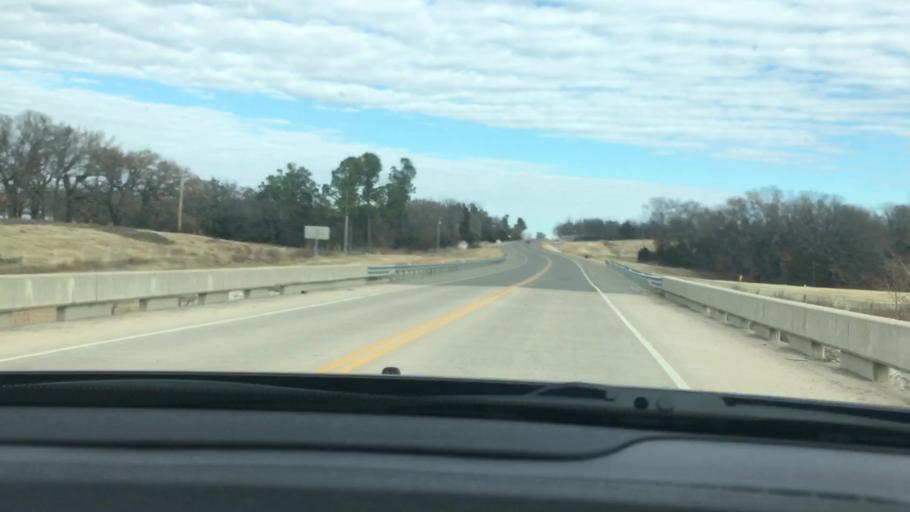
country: US
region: Oklahoma
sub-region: Garvin County
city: Pauls Valley
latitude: 34.7612
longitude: -97.1973
